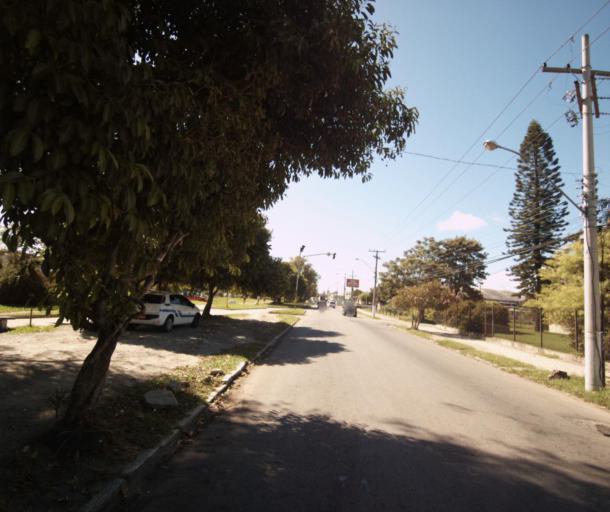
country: BR
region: Rio Grande do Sul
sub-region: Pelotas
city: Pelotas
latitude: -31.7636
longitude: -52.3570
